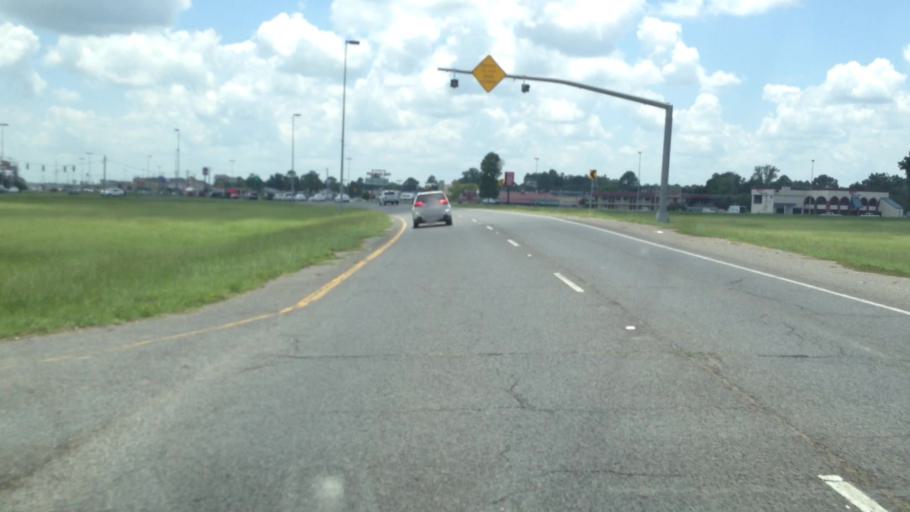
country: US
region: Louisiana
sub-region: Rapides Parish
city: Alexandria
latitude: 31.3009
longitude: -92.4803
